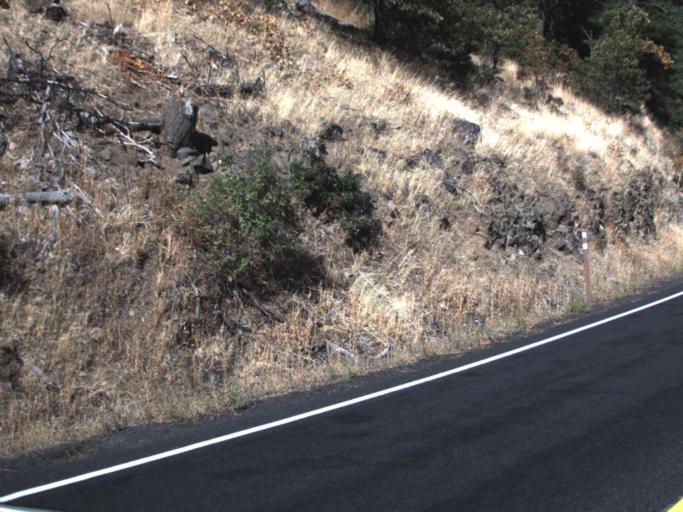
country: US
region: Washington
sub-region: Yakima County
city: Tieton
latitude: 46.6979
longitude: -120.8984
